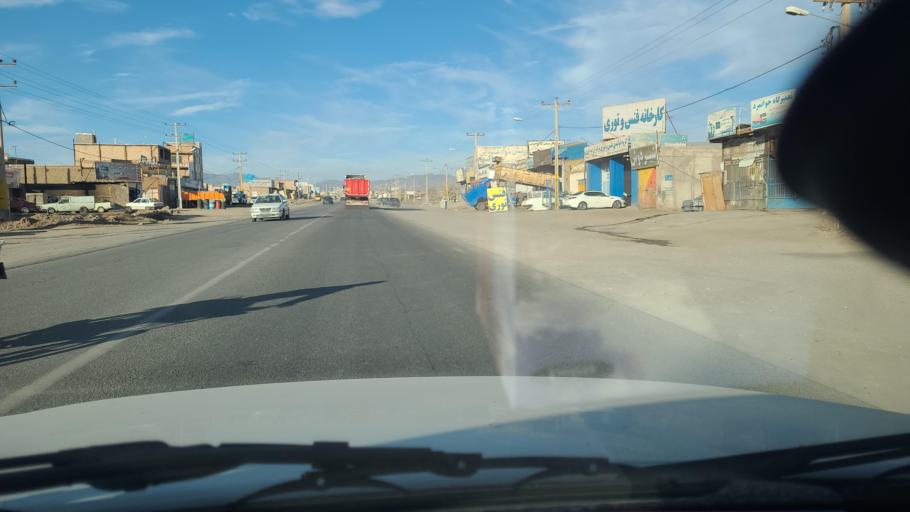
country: IR
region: Razavi Khorasan
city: Sabzevar
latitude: 36.2171
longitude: 57.6511
